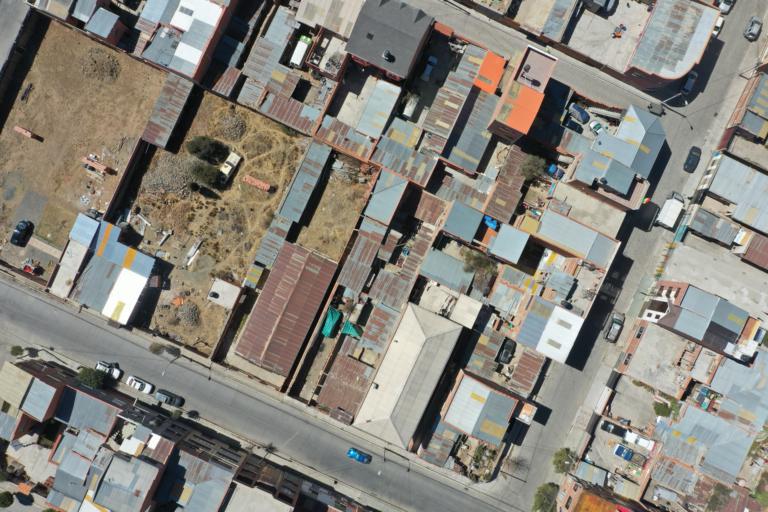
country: BO
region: La Paz
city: La Paz
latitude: -16.5337
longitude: -68.1510
